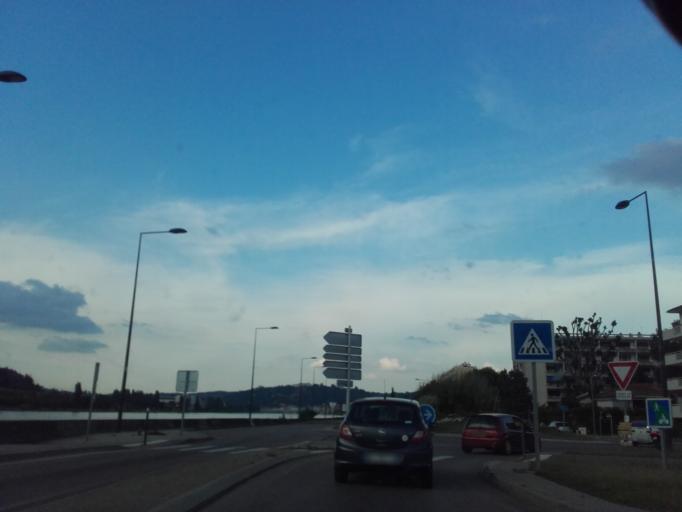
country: FR
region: Rhone-Alpes
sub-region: Departement du Rhone
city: Saint-Cyr-sur-le-Rhone
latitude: 45.5102
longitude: 4.8560
